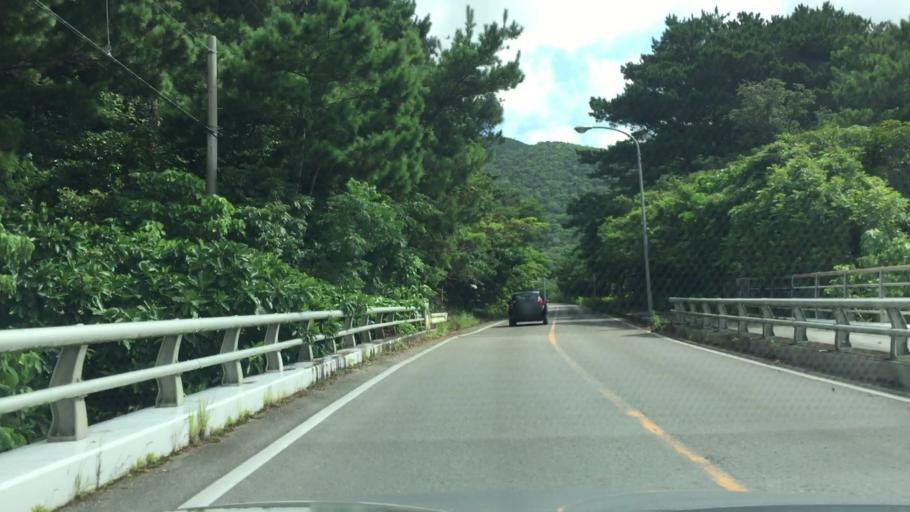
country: JP
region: Okinawa
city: Ishigaki
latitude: 24.4333
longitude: 124.2105
